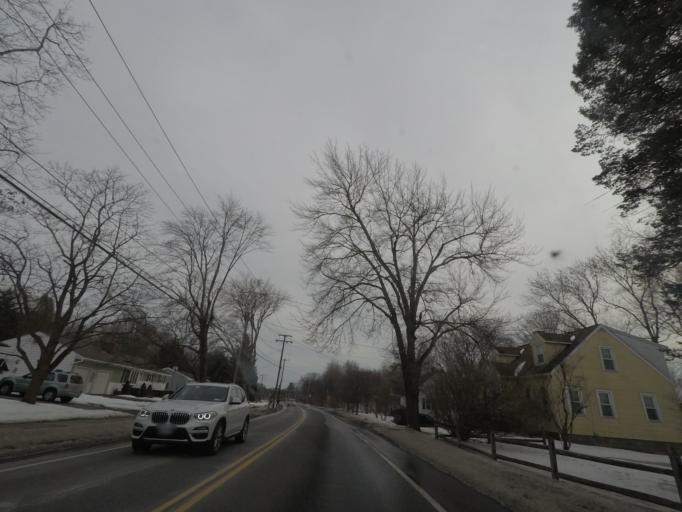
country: US
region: New York
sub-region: Albany County
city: Delmar
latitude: 42.6086
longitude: -73.8448
